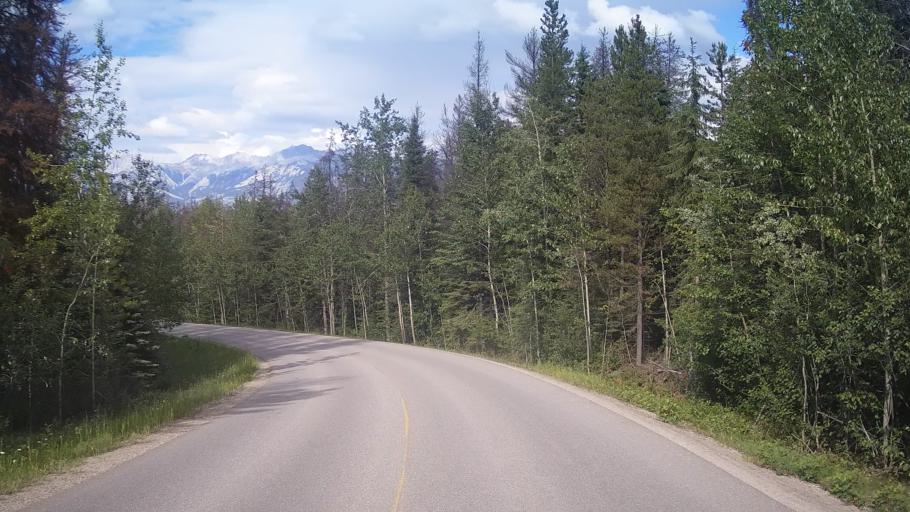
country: CA
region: Alberta
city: Jasper Park Lodge
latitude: 52.8526
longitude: -118.1040
